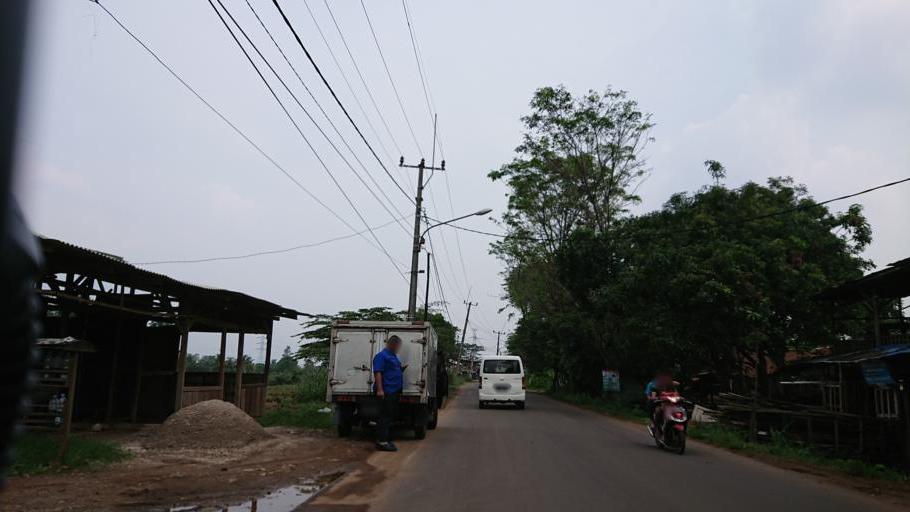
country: ID
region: West Java
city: Parung
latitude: -6.4555
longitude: 106.7051
